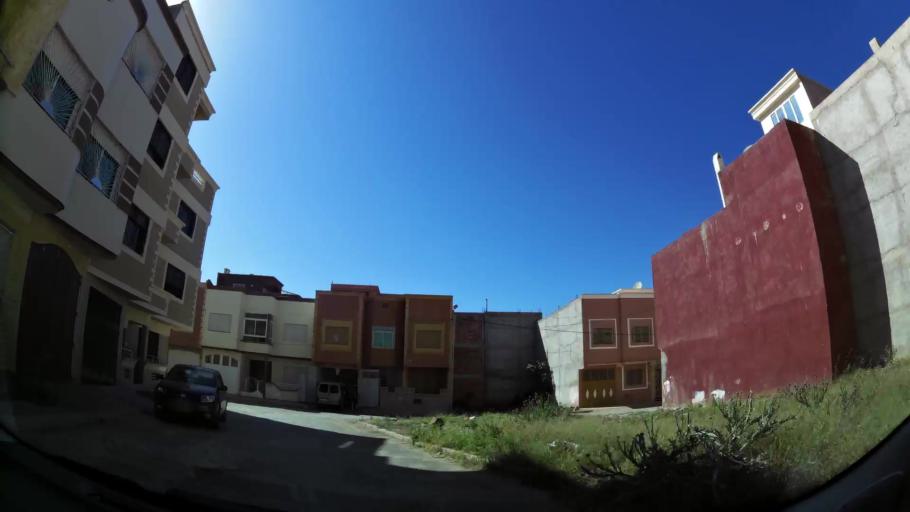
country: MA
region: Oriental
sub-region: Berkane-Taourirt
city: Berkane
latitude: 34.9413
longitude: -2.3407
